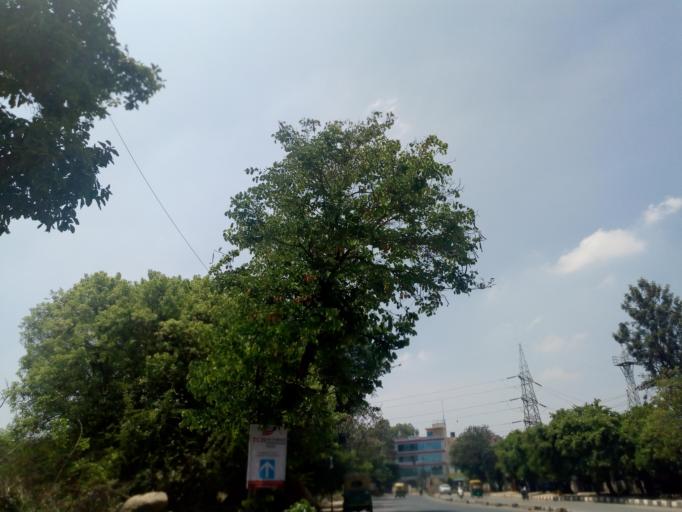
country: IN
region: Karnataka
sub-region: Bangalore Urban
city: Bangalore
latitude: 12.9031
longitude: 77.6506
